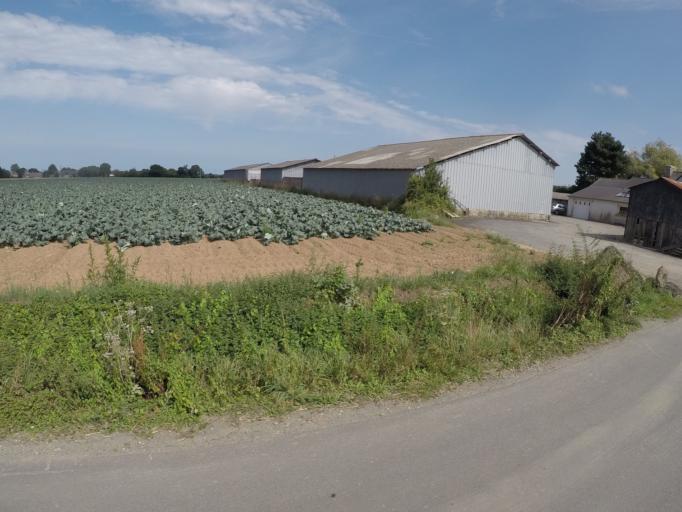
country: FR
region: Brittany
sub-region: Departement des Cotes-d'Armor
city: Goudelin
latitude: 48.5992
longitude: -3.0121
